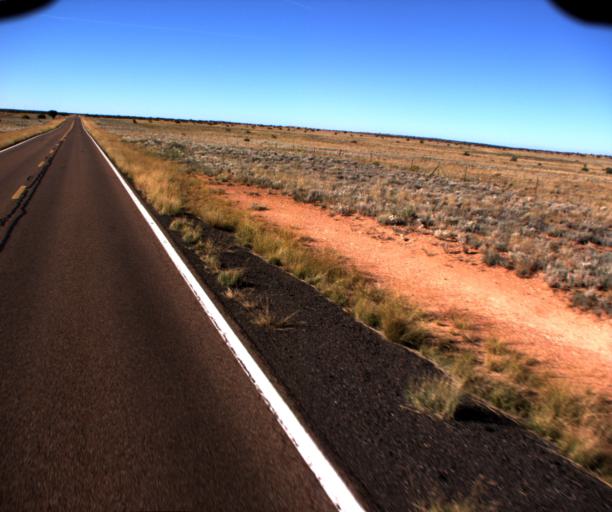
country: US
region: Arizona
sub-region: Navajo County
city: Holbrook
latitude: 34.7153
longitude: -110.2968
